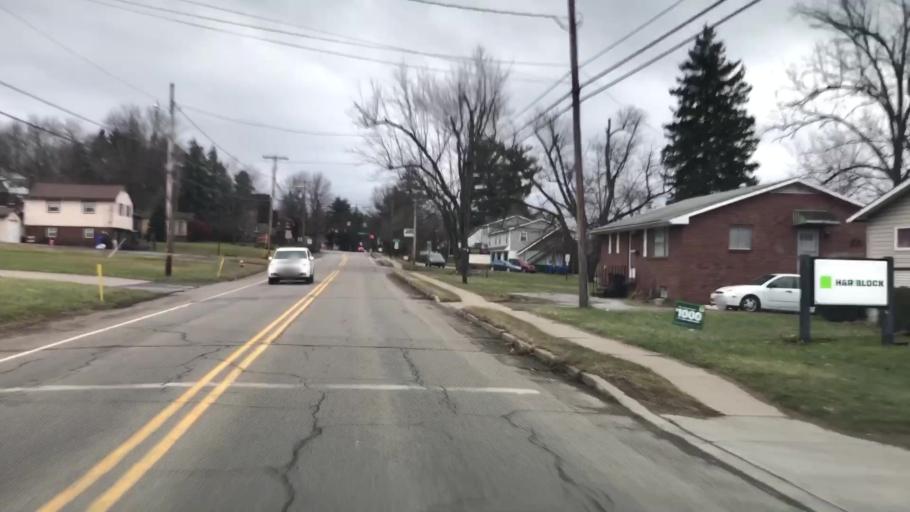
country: US
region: Pennsylvania
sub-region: Butler County
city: Slippery Rock
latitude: 41.0689
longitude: -80.0520
